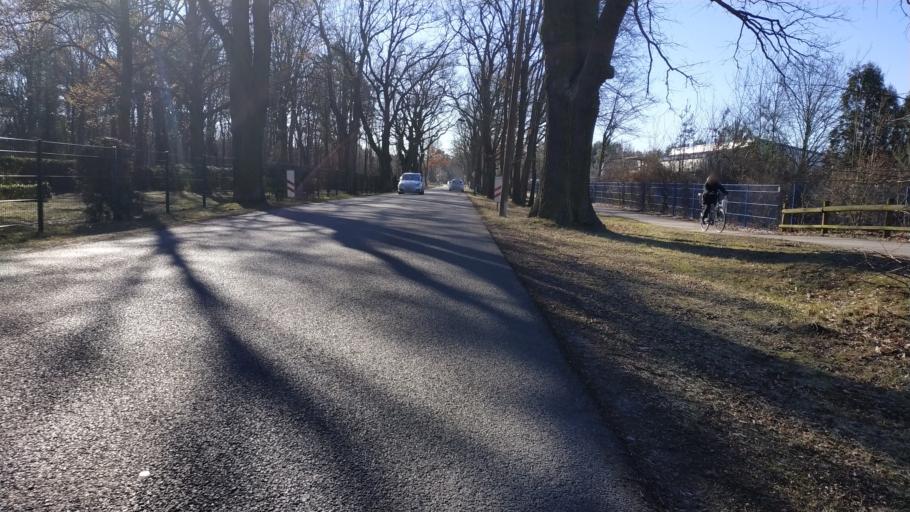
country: DE
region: Brandenburg
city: Petershagen
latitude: 52.5326
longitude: 13.8109
